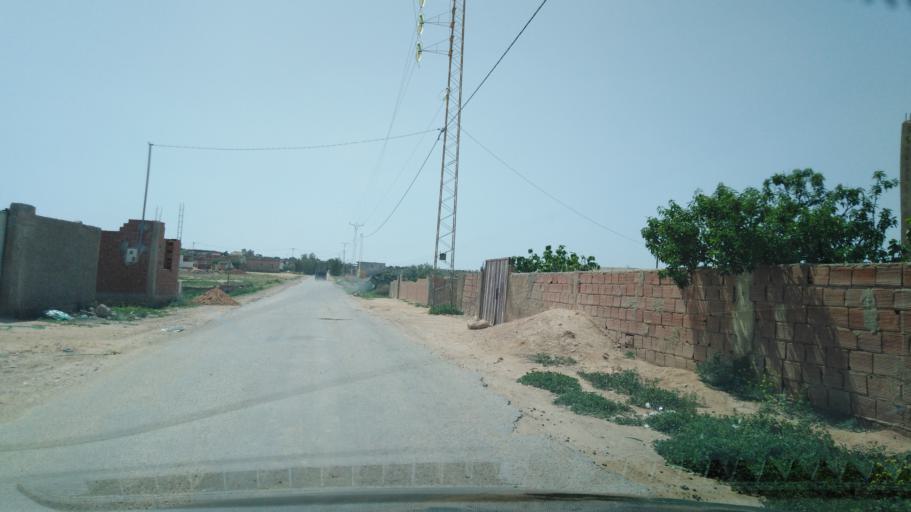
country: TN
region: Safaqis
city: Sfax
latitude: 34.7268
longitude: 10.5291
